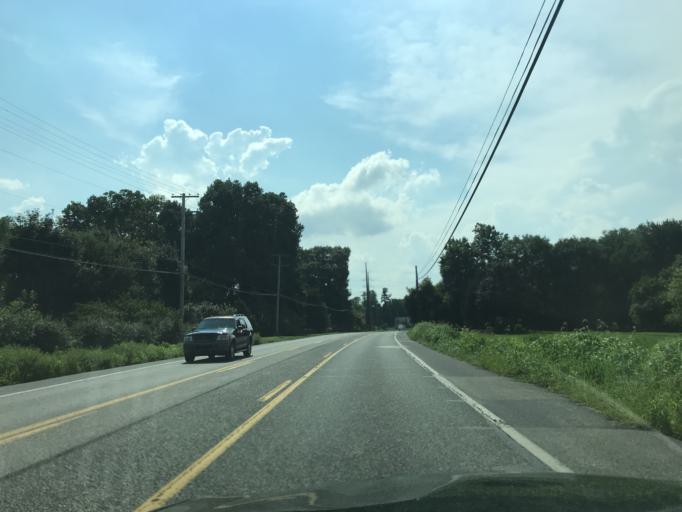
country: US
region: Pennsylvania
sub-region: Lancaster County
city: Mountville
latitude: 40.0323
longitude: -76.4664
